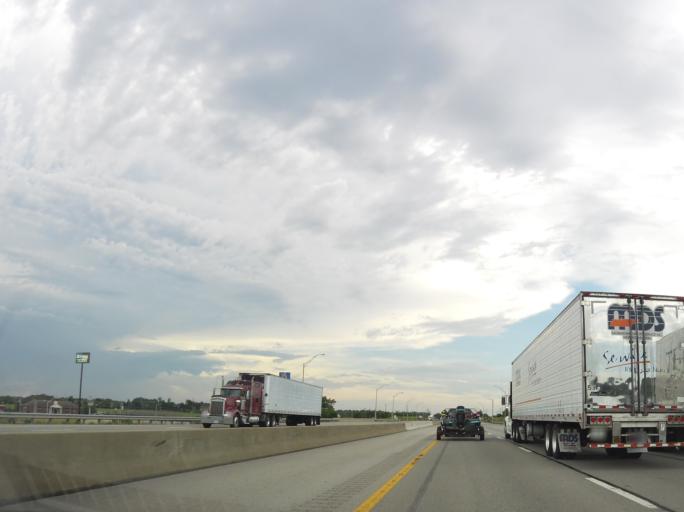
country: US
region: Kentucky
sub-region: Madison County
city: Berea
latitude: 37.5958
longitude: -84.3143
